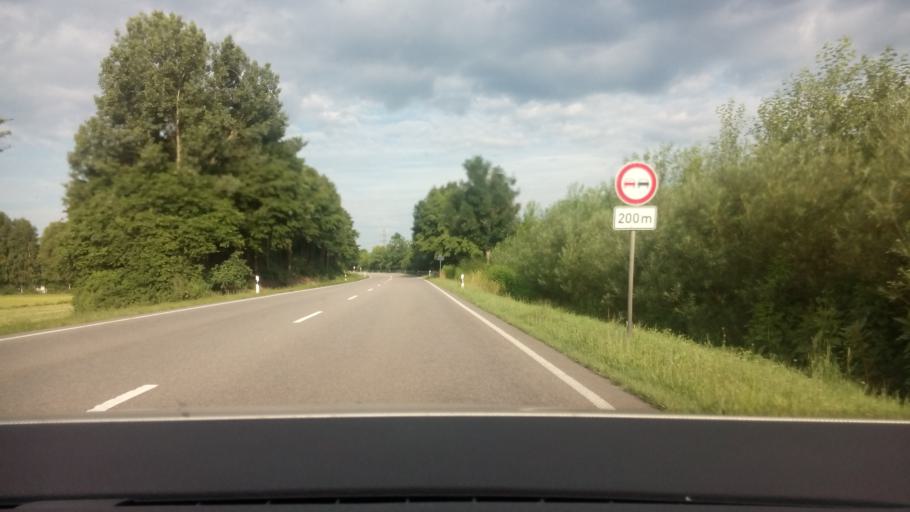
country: DE
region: Bavaria
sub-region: Upper Bavaria
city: Karlsfeld
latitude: 48.2424
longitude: 11.4618
